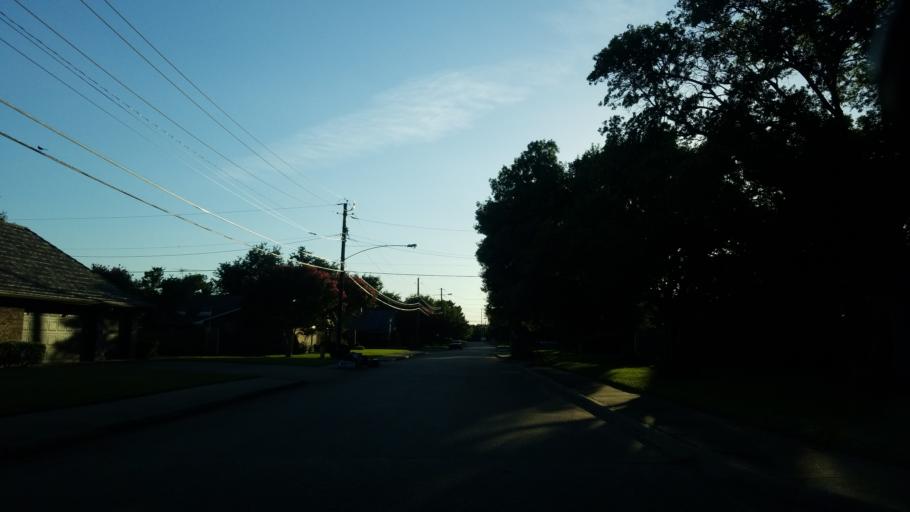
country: US
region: Texas
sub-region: Dallas County
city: Balch Springs
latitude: 32.7885
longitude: -96.6956
